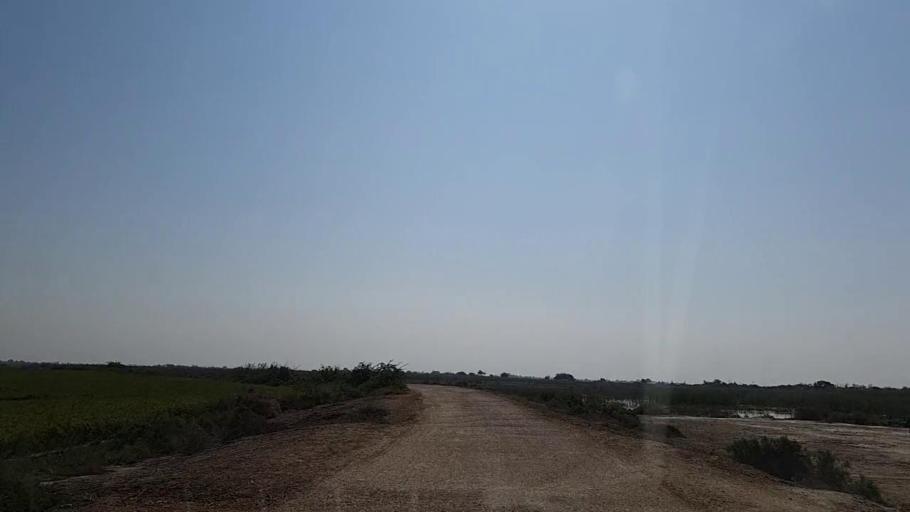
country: PK
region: Sindh
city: Chuhar Jamali
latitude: 24.4695
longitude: 68.0931
